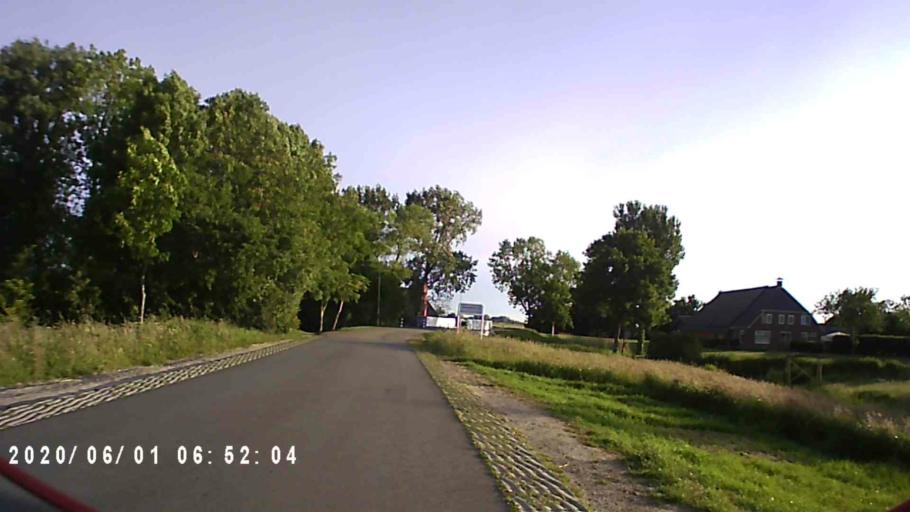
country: NL
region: Friesland
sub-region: Gemeente Kollumerland en Nieuwkruisland
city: Kollum
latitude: 53.3074
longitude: 6.1314
